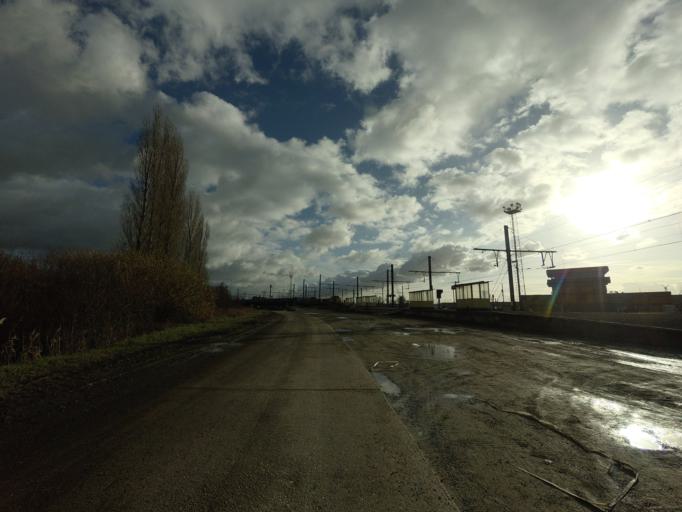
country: BE
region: Flanders
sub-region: Provincie Antwerpen
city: Stabroek
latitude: 51.2923
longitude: 4.3782
